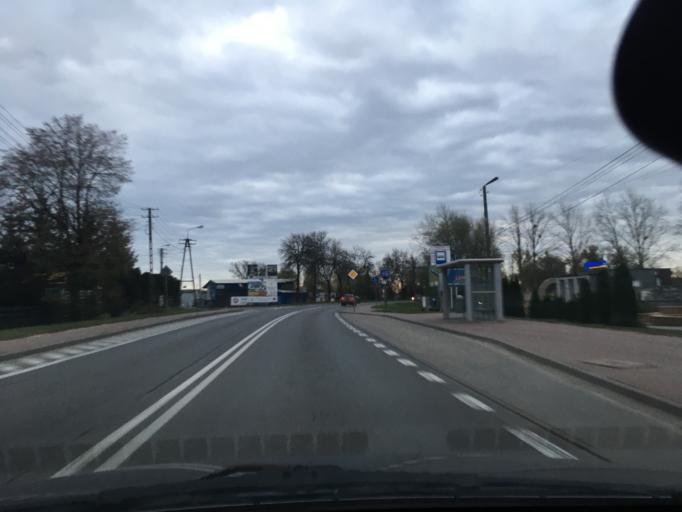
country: PL
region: Masovian Voivodeship
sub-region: Powiat piaseczynski
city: Lesznowola
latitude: 52.0910
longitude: 20.9339
